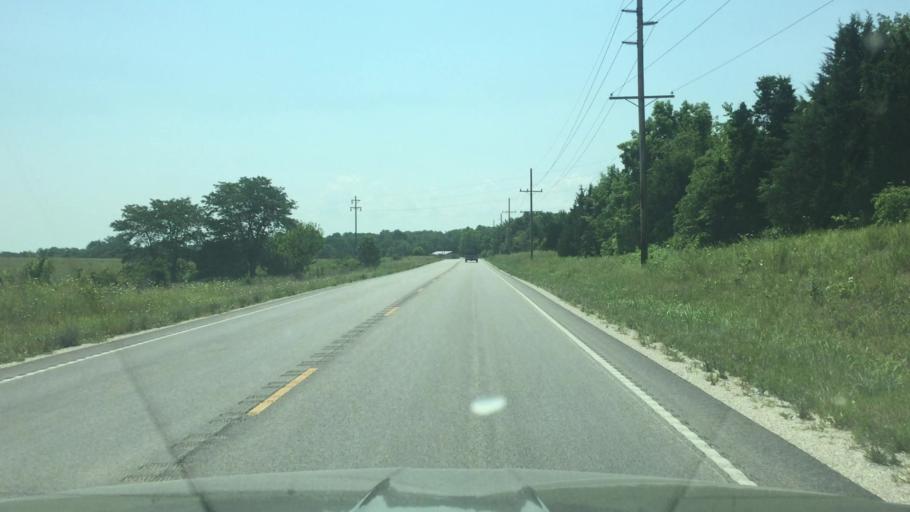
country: US
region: Missouri
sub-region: Miller County
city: Eldon
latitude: 38.3834
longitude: -92.6850
